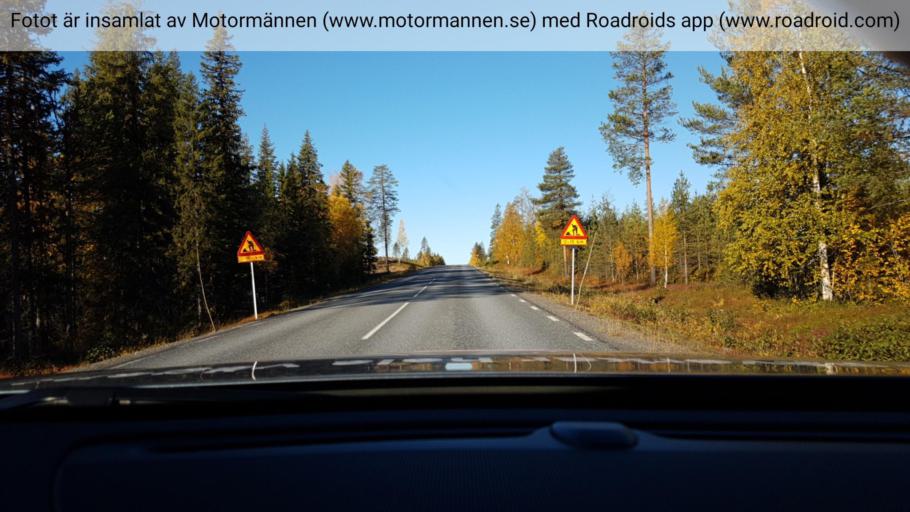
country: SE
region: Vaesterbotten
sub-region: Skelleftea Kommun
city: Langsele
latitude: 65.3842
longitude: 20.0874
